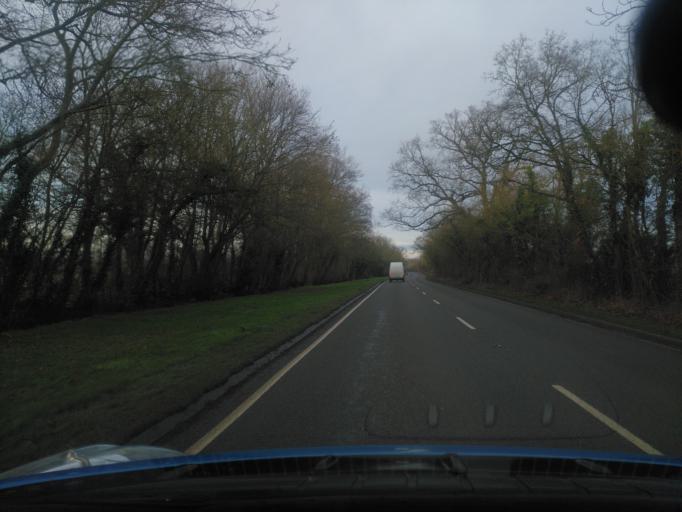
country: GB
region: England
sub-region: Gloucestershire
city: Moreton in Marsh
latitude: 51.9827
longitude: -1.6539
